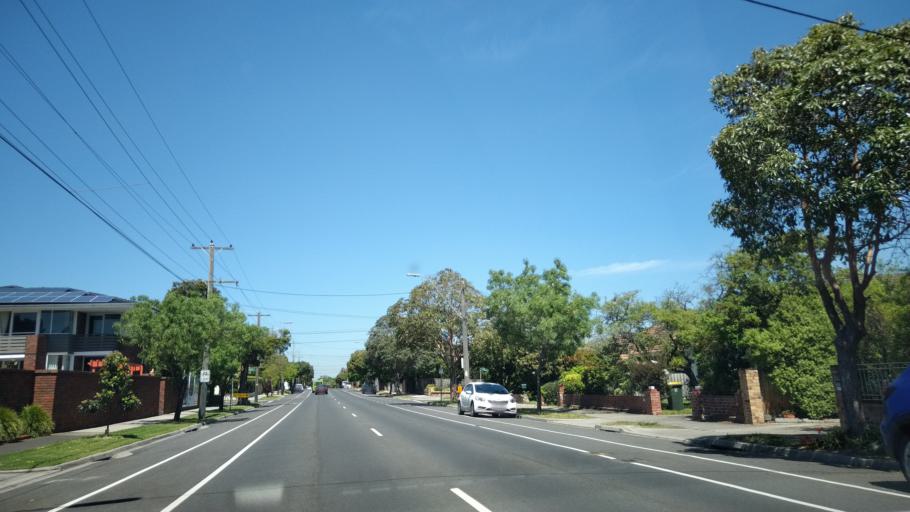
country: AU
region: Victoria
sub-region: Glen Eira
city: Caulfield South
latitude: -37.8982
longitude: 145.0268
